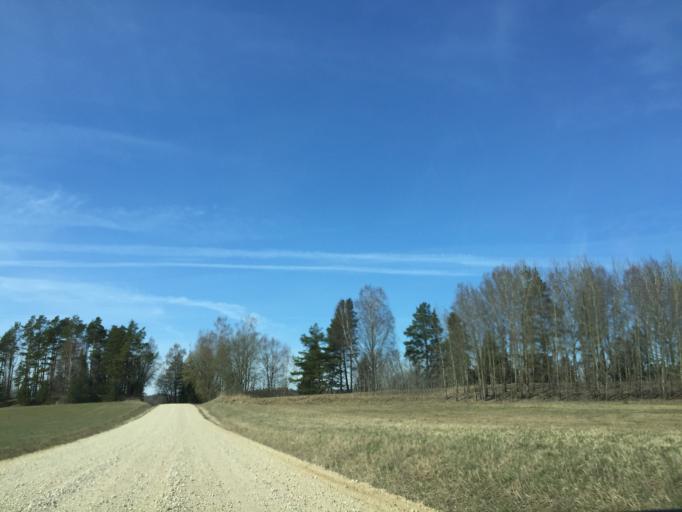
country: EE
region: Vorumaa
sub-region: Antsla vald
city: Vana-Antsla
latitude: 57.9525
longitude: 26.3665
